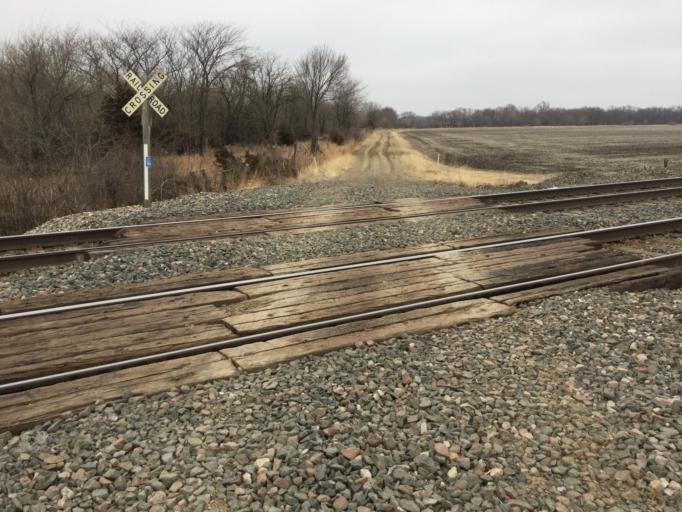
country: US
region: Kansas
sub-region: Franklin County
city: Ottawa
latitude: 38.6564
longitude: -95.2302
